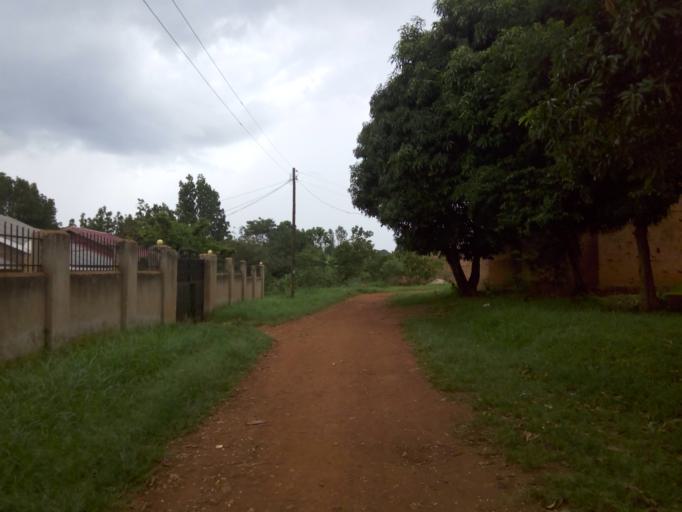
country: UG
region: Western Region
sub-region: Masindi District
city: Masindi
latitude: 1.6809
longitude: 31.7144
